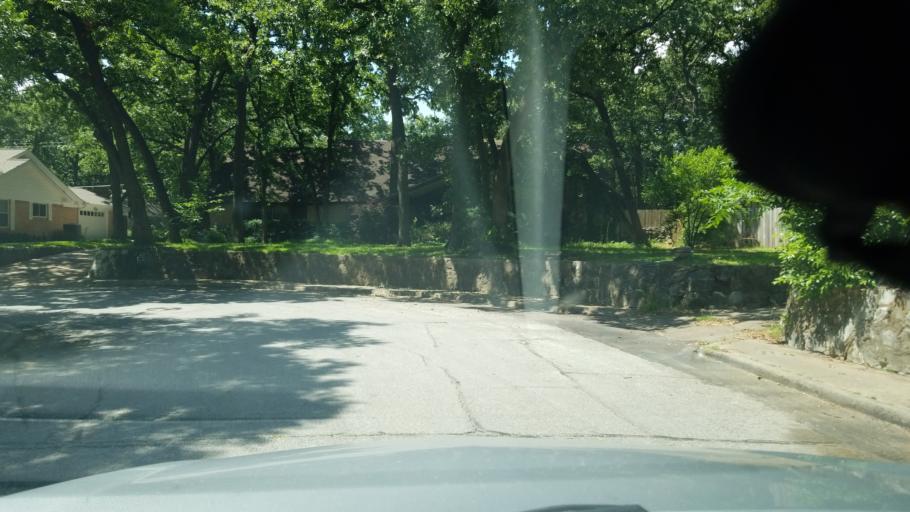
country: US
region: Texas
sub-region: Dallas County
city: Irving
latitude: 32.8307
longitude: -96.9544
